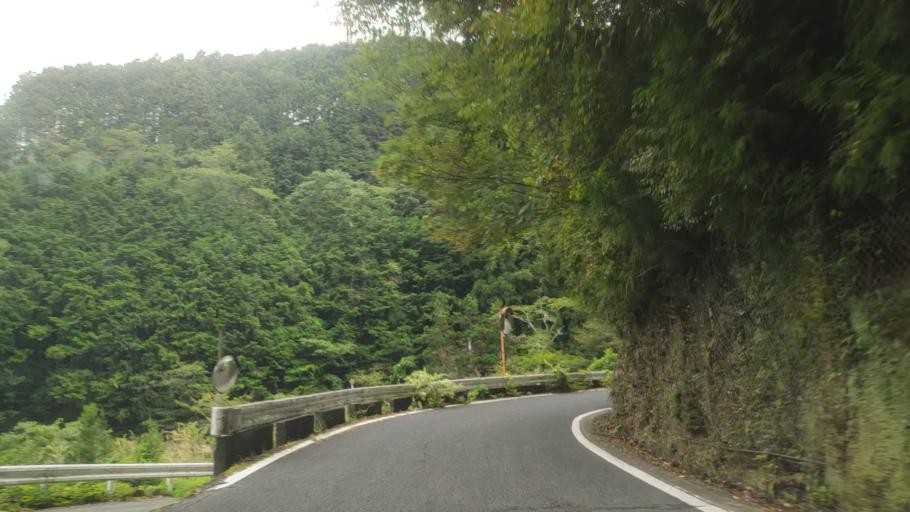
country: JP
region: Wakayama
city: Koya
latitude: 34.2384
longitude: 135.5465
